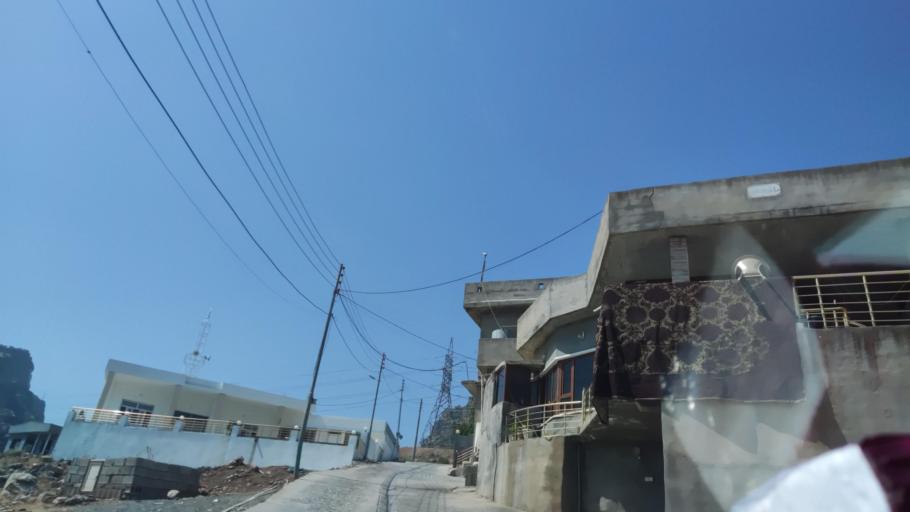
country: IQ
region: Arbil
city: Ruwandiz
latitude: 36.6488
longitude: 44.4957
